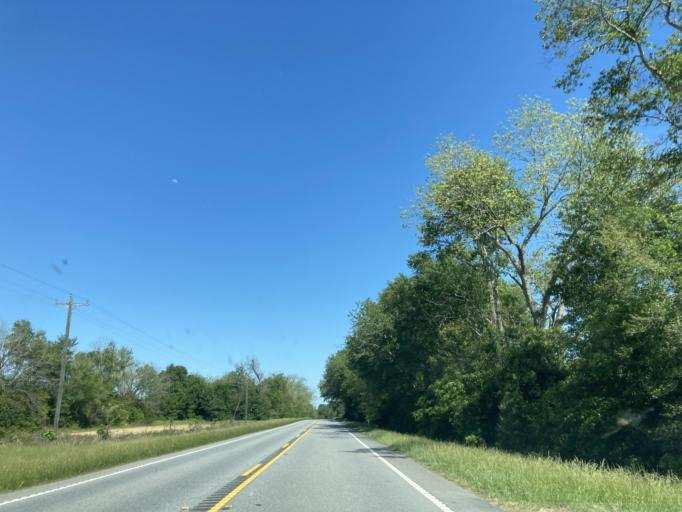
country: US
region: Georgia
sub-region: Miller County
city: Colquitt
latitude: 31.1835
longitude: -84.5487
